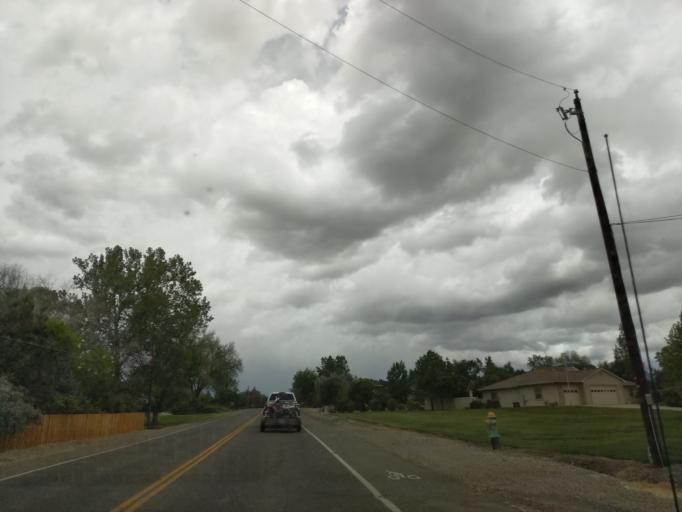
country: US
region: Colorado
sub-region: Mesa County
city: Grand Junction
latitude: 39.0990
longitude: -108.5616
